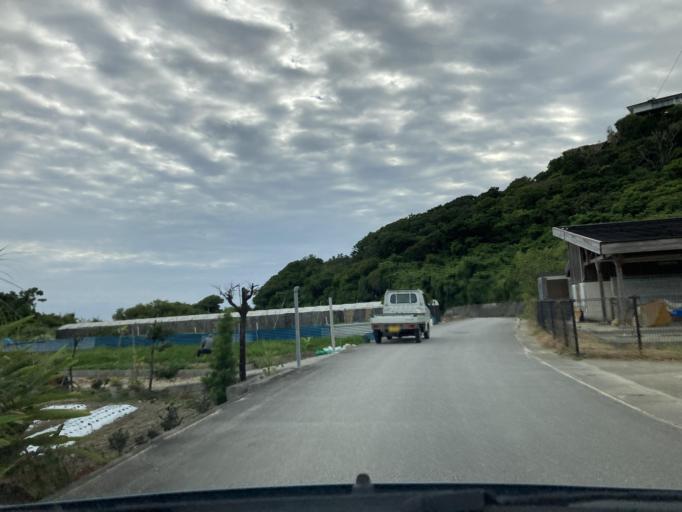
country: JP
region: Okinawa
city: Tomigusuku
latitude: 26.1373
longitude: 127.7935
